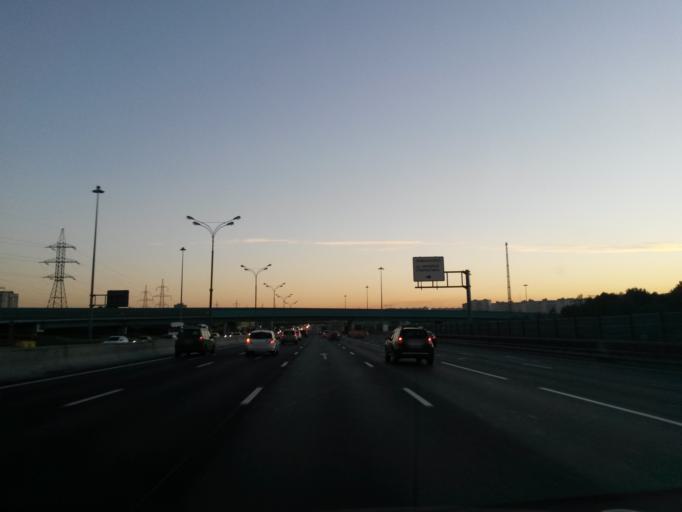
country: RU
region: Moskovskaya
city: Kuskovo
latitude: 55.7283
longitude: 37.8401
